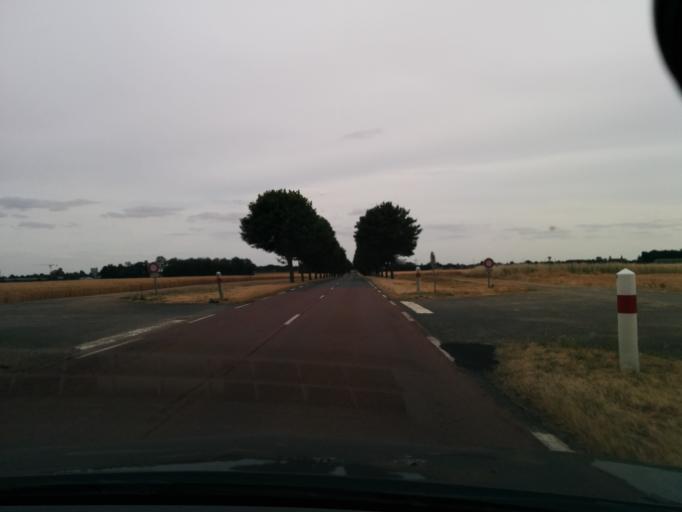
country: FR
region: Ile-de-France
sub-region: Departement de l'Essonne
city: Angerville
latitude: 48.3282
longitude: 1.9931
